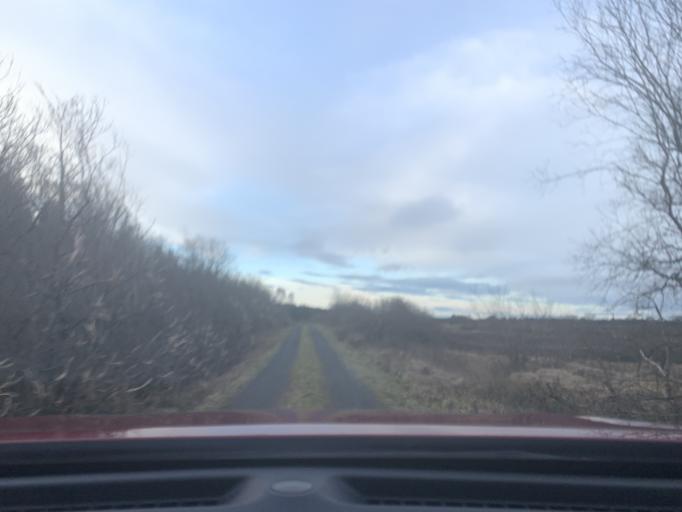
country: IE
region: Connaught
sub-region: Roscommon
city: Ballaghaderreen
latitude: 53.8880
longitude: -8.5788
